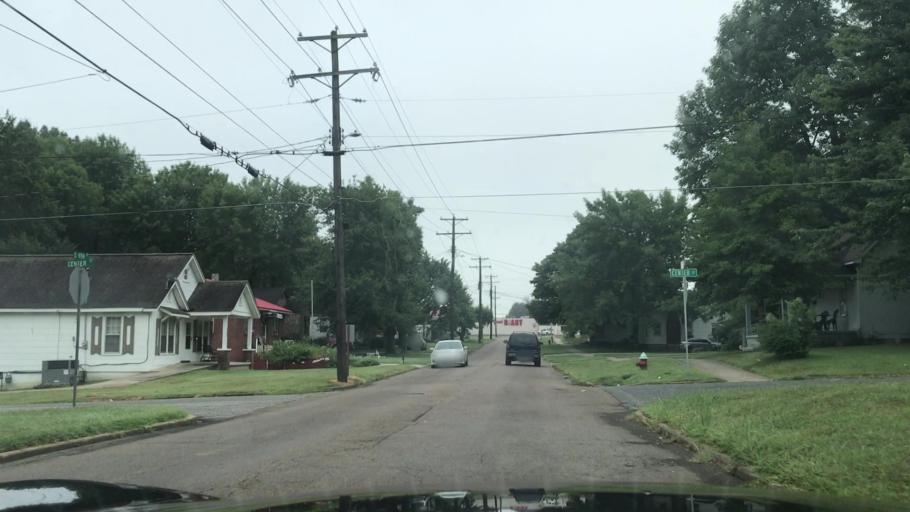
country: US
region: Kentucky
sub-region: Graves County
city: Mayfield
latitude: 36.7317
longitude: -88.6388
